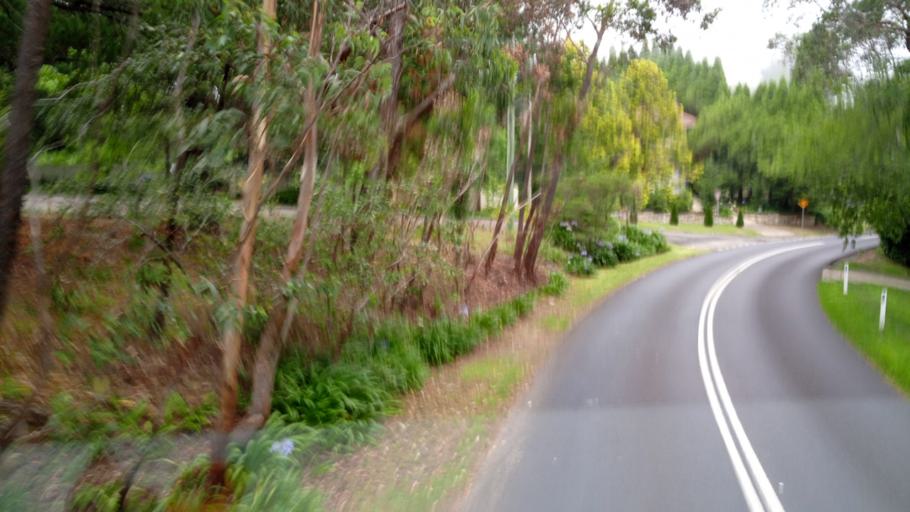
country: AU
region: New South Wales
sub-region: Blue Mountains Municipality
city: Leura
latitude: -33.7161
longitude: 150.3405
